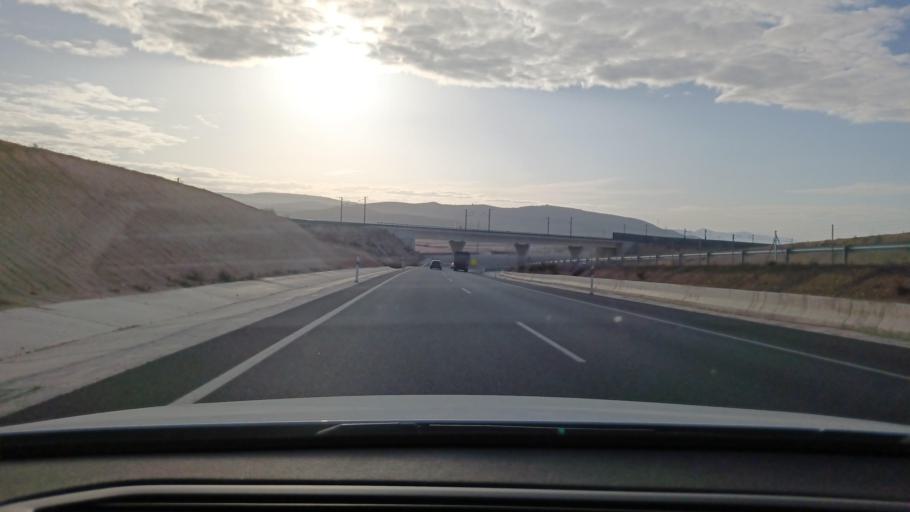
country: ES
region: Castille-La Mancha
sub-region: Provincia de Albacete
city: Caudete
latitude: 38.7206
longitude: -0.9348
